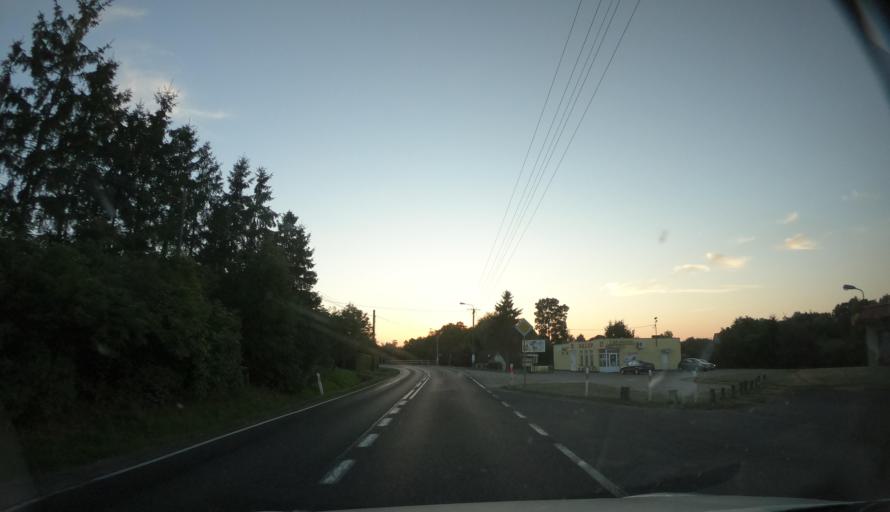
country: PL
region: Kujawsko-Pomorskie
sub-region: Powiat bydgoski
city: Koronowo
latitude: 53.3278
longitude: 17.9049
